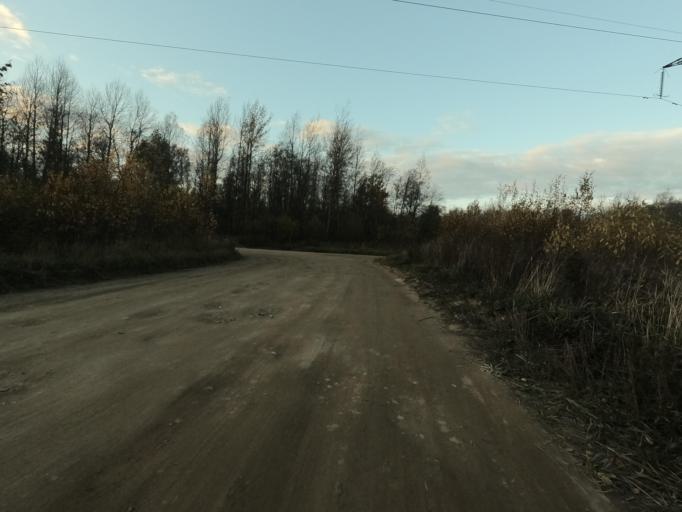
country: RU
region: Leningrad
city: Mga
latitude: 59.8063
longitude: 31.2011
